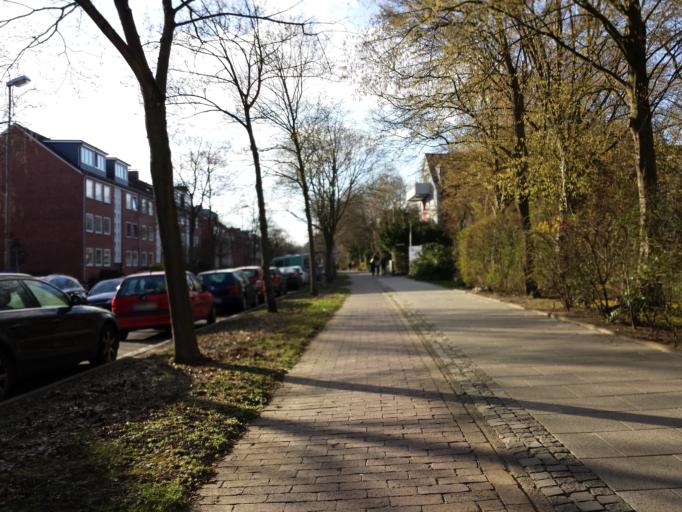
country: DE
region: Bremen
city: Bremen
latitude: 53.0974
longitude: 8.8453
